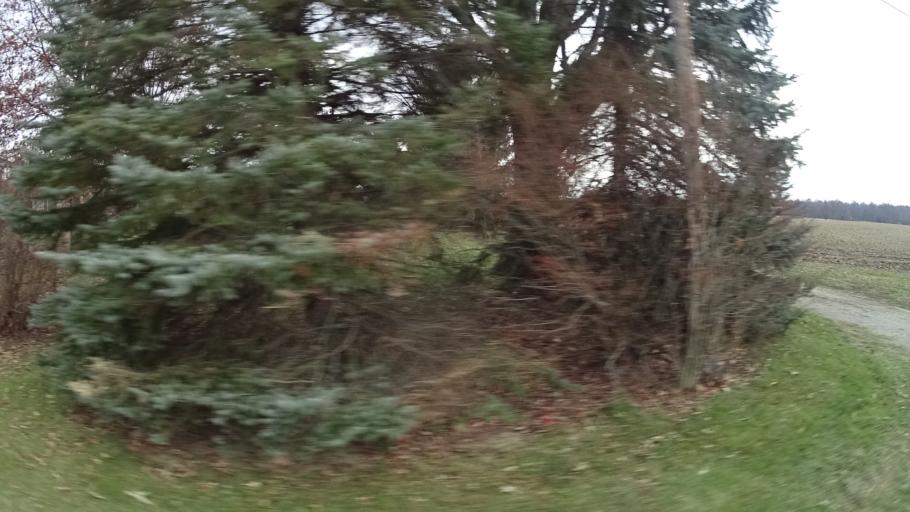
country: US
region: Ohio
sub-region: Lorain County
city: Wellington
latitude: 41.1825
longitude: -82.1689
